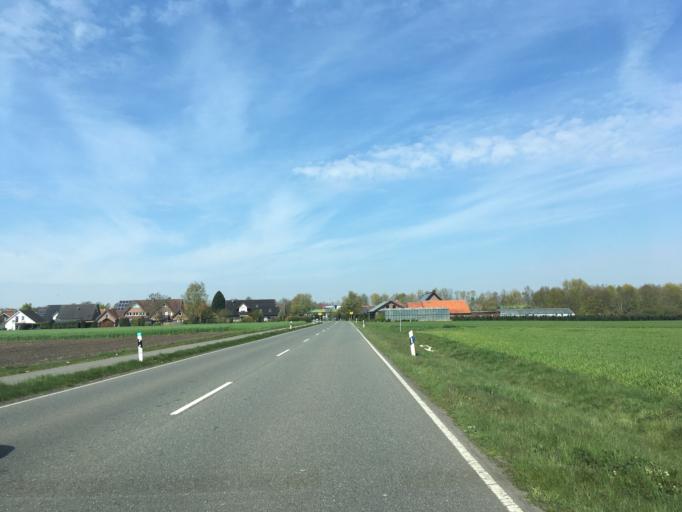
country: DE
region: North Rhine-Westphalia
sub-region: Regierungsbezirk Munster
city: Vreden
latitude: 52.0221
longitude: 6.8342
